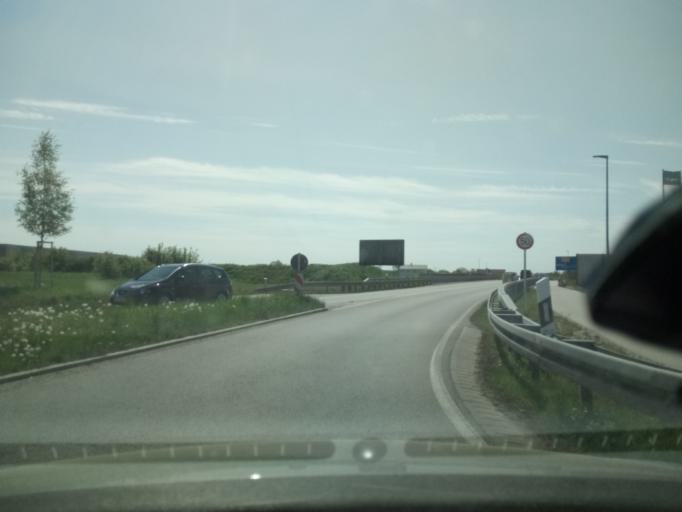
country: DE
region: Bavaria
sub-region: Upper Bavaria
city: Ampfing
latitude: 48.2472
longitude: 12.4123
